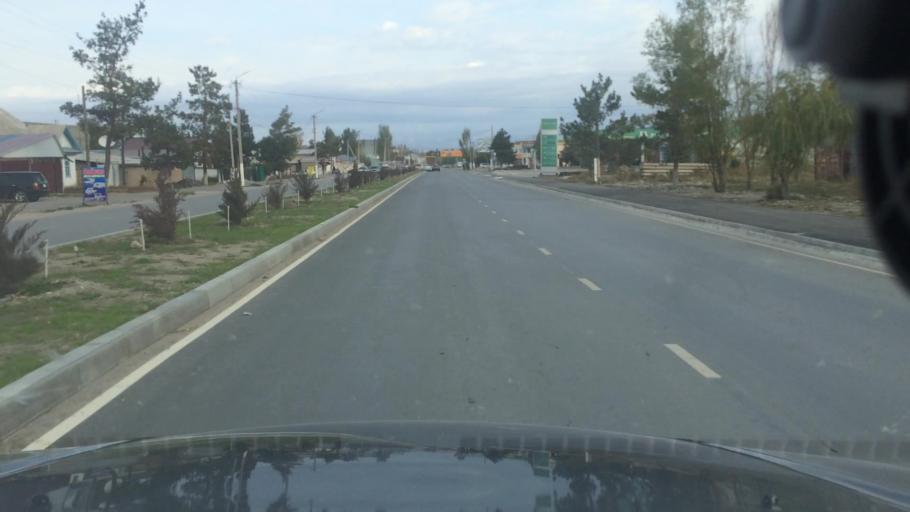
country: KG
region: Ysyk-Koel
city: Karakol
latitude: 42.5096
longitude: 78.3857
